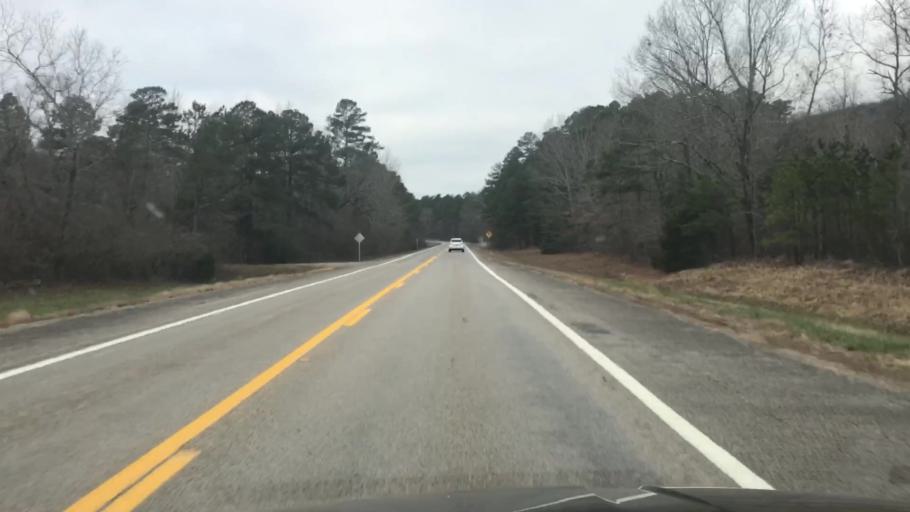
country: US
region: Arkansas
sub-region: Montgomery County
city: Mount Ida
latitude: 34.6860
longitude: -93.8576
